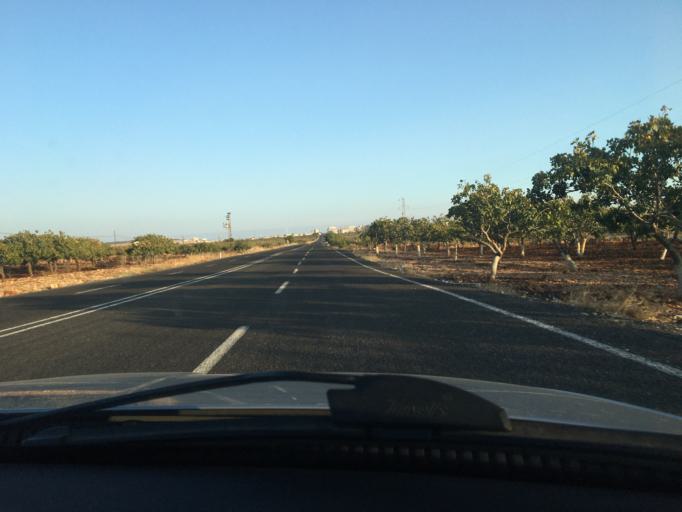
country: TR
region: Sanliurfa
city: Halfeti
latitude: 37.2389
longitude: 37.9175
